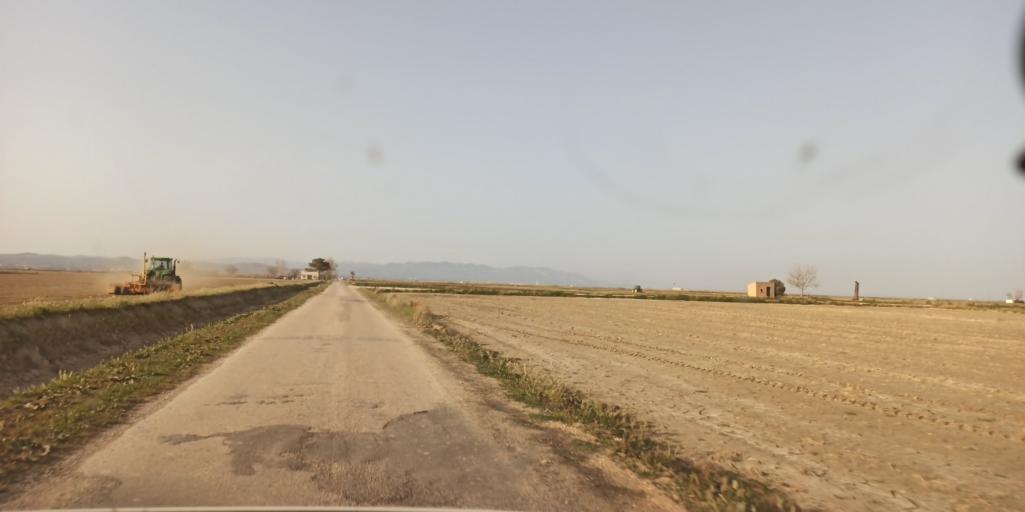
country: ES
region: Catalonia
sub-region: Provincia de Tarragona
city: Deltebre
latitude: 40.7570
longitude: 0.7539
